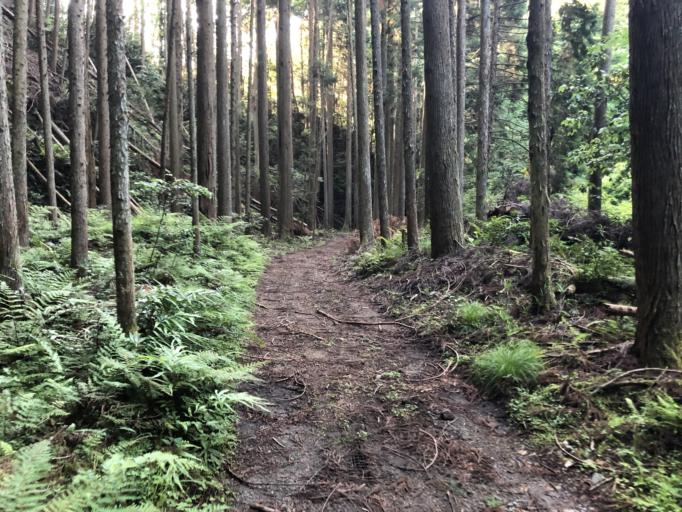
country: JP
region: Kyoto
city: Kameoka
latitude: 34.9859
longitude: 135.6255
